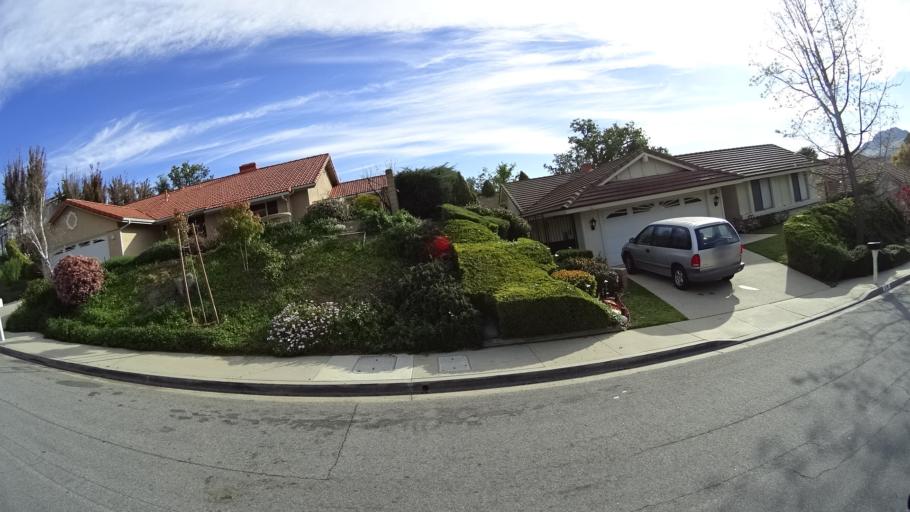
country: US
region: California
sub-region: Ventura County
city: Thousand Oaks
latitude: 34.1552
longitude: -118.8330
